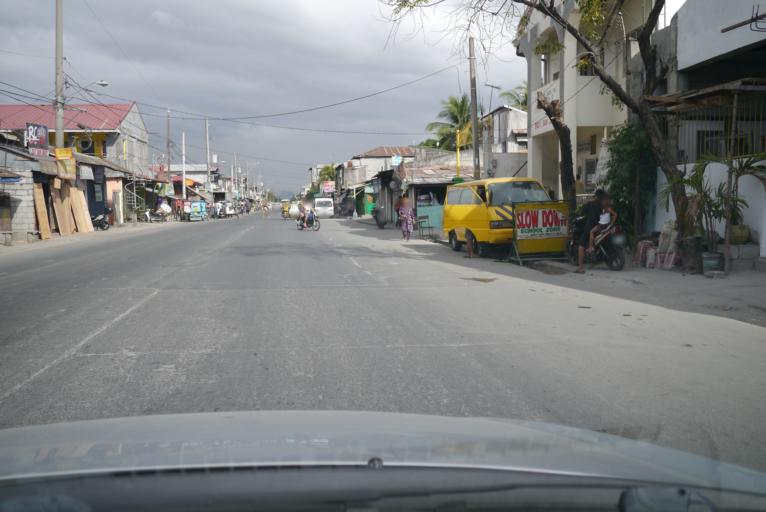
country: PH
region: Calabarzon
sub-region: Province of Rizal
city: Taytay
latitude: 14.5548
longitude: 121.1168
